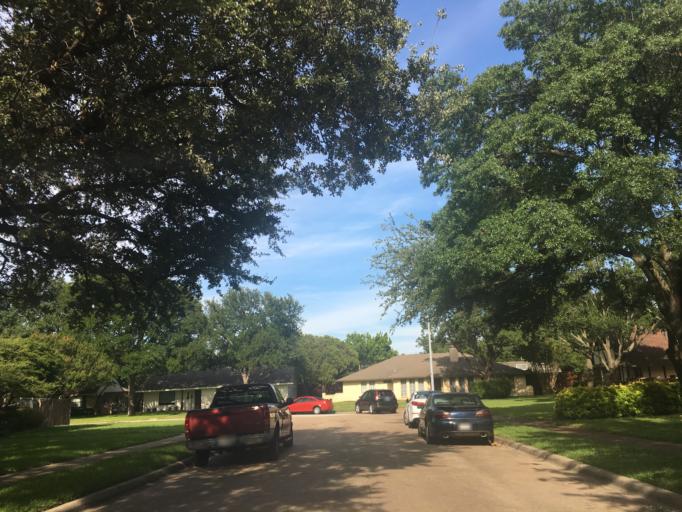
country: US
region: Texas
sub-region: Dallas County
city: Richardson
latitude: 32.9408
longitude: -96.7166
